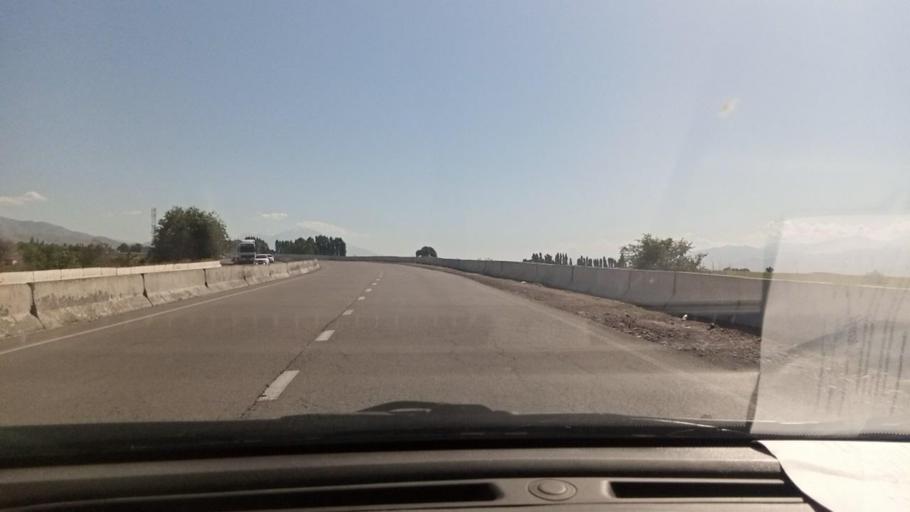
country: UZ
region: Toshkent
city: Angren
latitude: 40.9410
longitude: 69.9048
